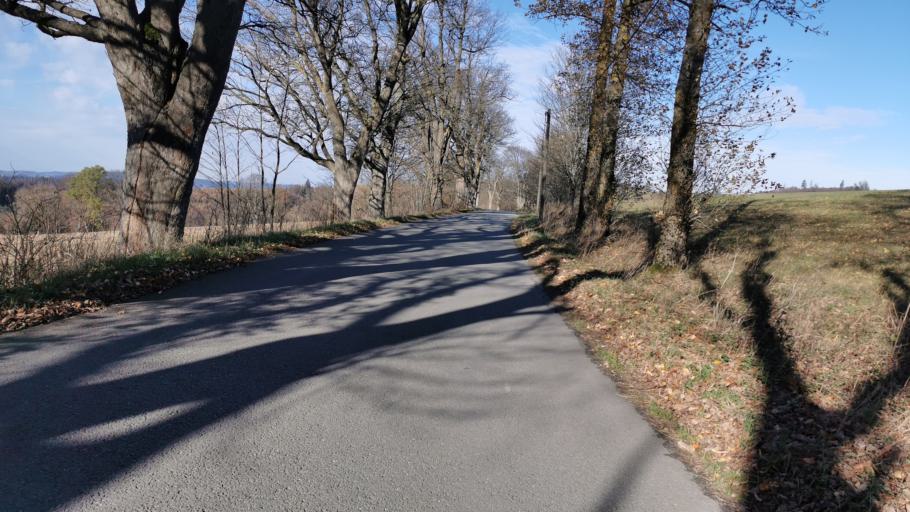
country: DE
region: Bavaria
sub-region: Upper Franconia
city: Ludwigsstadt
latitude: 50.4680
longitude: 11.4367
